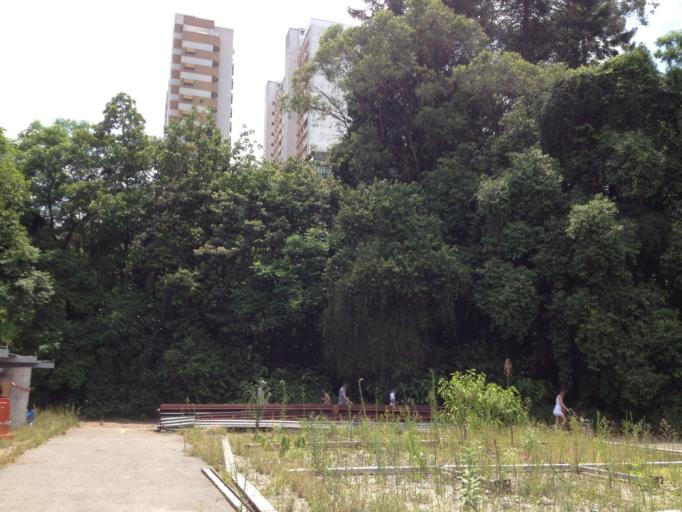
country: BR
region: Sao Paulo
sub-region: Sao Paulo
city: Sao Paulo
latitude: -23.5501
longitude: -46.6490
